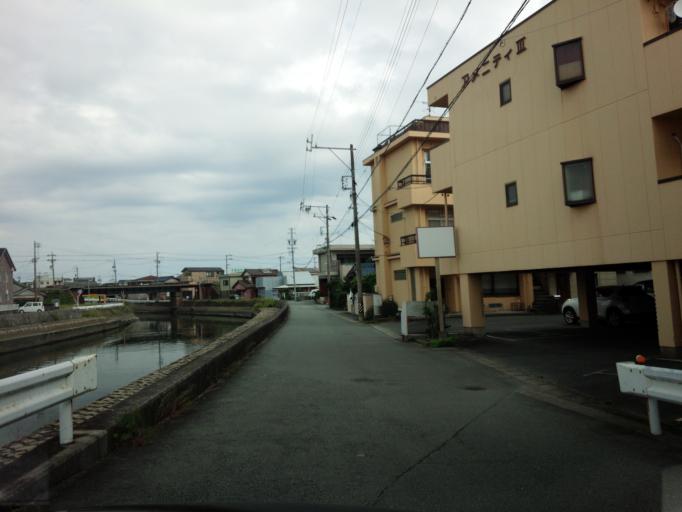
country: JP
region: Mie
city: Ise
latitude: 34.4892
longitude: 136.7169
